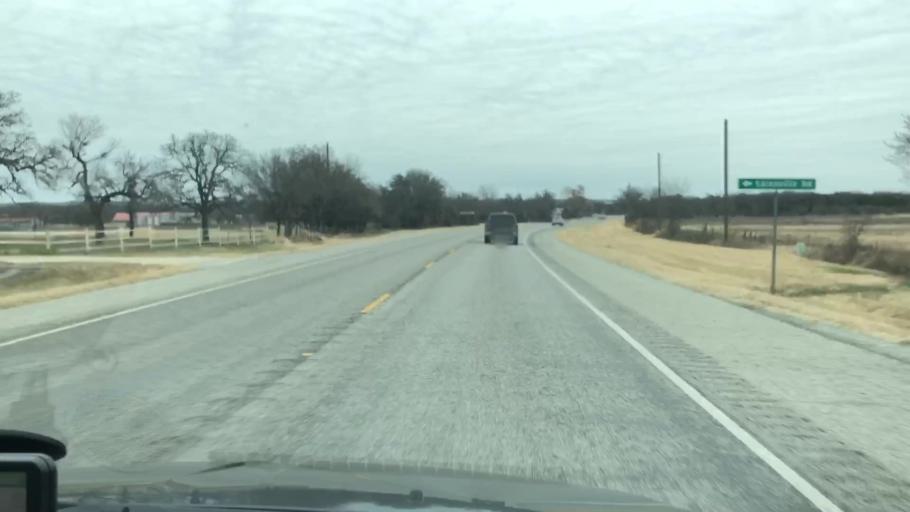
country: US
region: Texas
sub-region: Palo Pinto County
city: Mineral Wells
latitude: 32.8895
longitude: -98.0882
